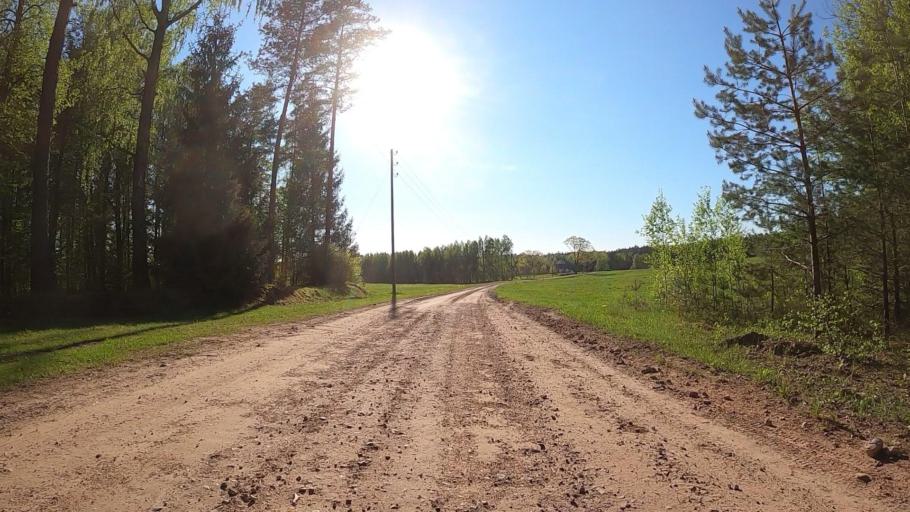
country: LV
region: Baldone
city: Baldone
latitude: 56.7620
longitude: 24.3780
